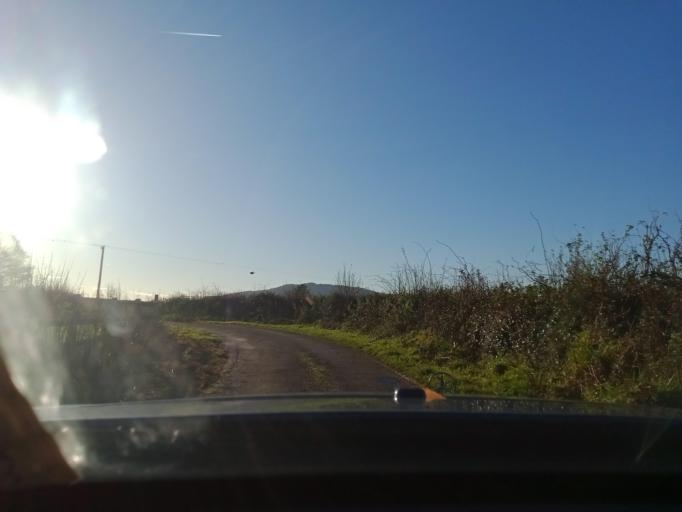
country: IE
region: Munster
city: Carrick-on-Suir
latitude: 52.4356
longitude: -7.3934
